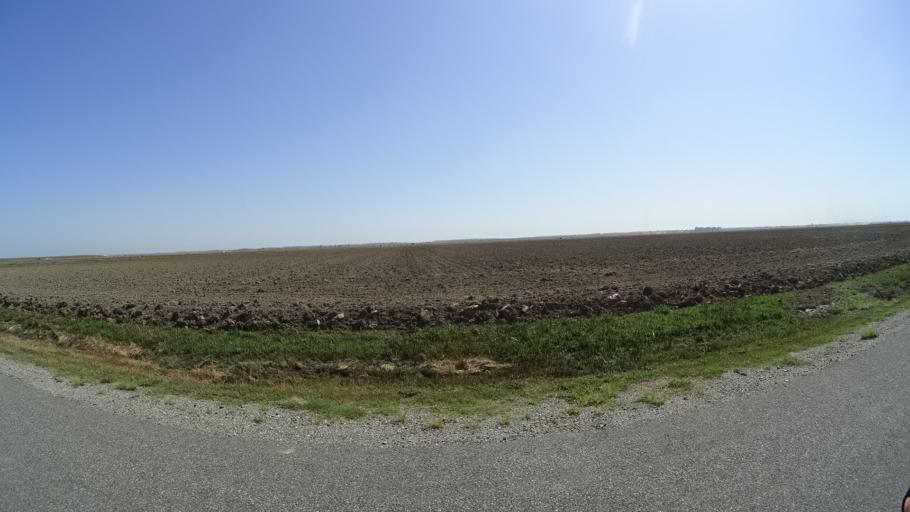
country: US
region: California
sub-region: Glenn County
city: Willows
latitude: 39.5062
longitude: -122.0653
